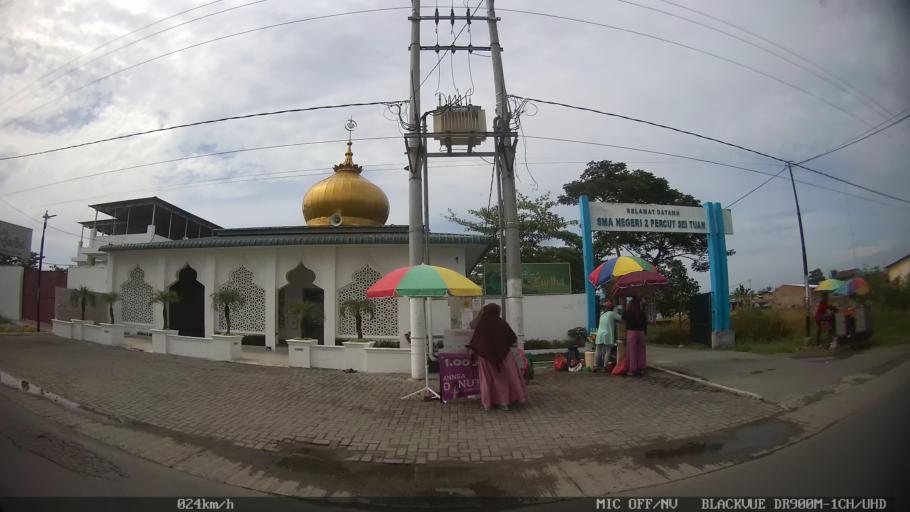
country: ID
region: North Sumatra
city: Medan
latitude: 3.6200
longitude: 98.7613
